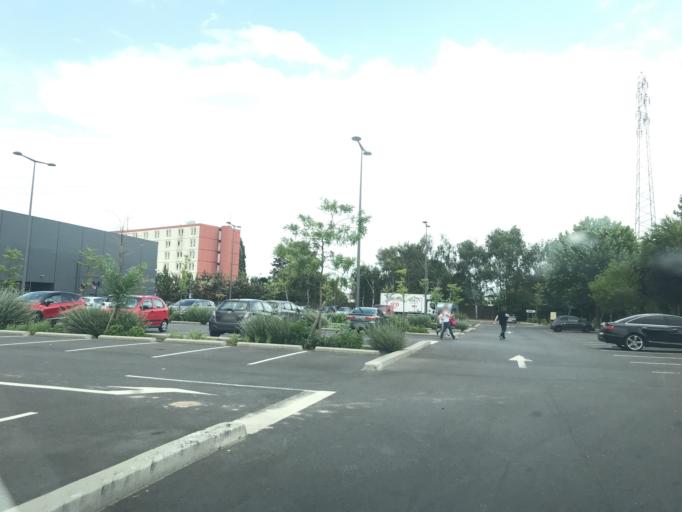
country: FR
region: Ile-de-France
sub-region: Departement des Yvelines
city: Maurepas
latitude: 48.7571
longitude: 1.9357
